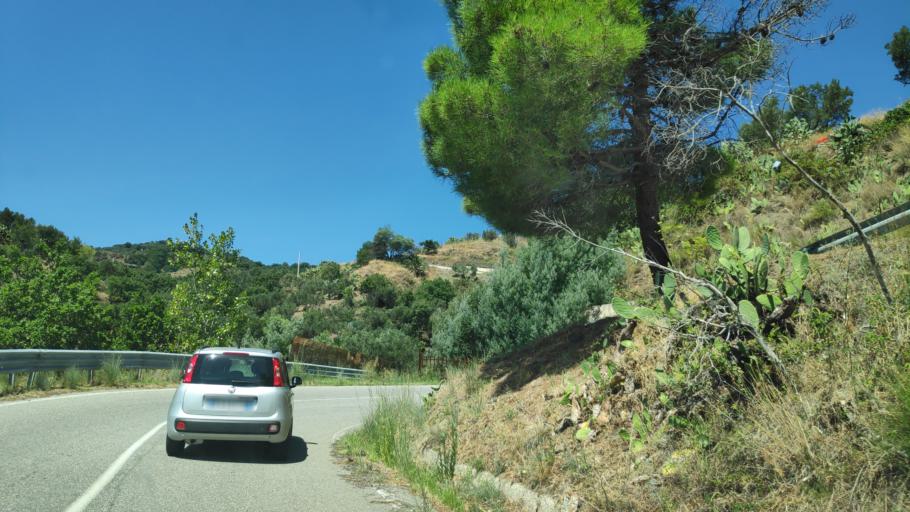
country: IT
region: Calabria
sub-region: Provincia di Catanzaro
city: Montauro
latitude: 38.7461
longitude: 16.5179
